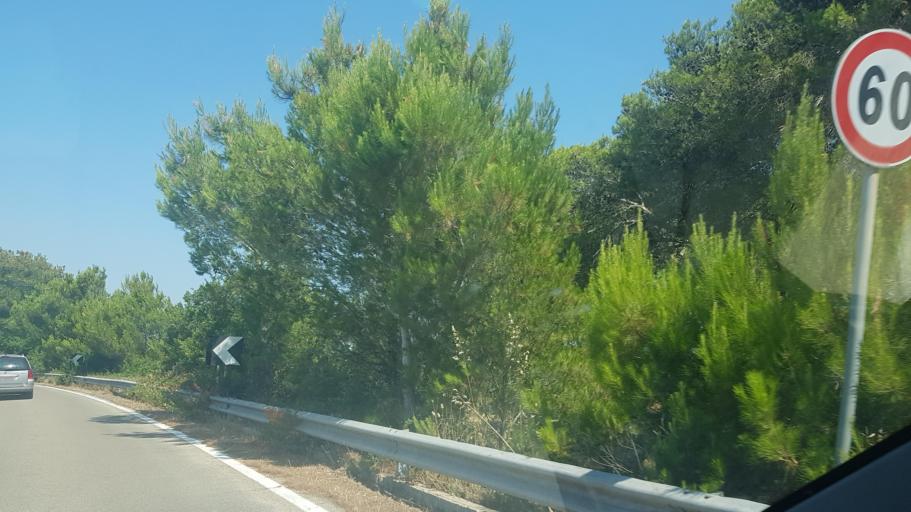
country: IT
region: Apulia
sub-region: Provincia di Lecce
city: Borgagne
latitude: 40.2076
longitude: 18.4305
